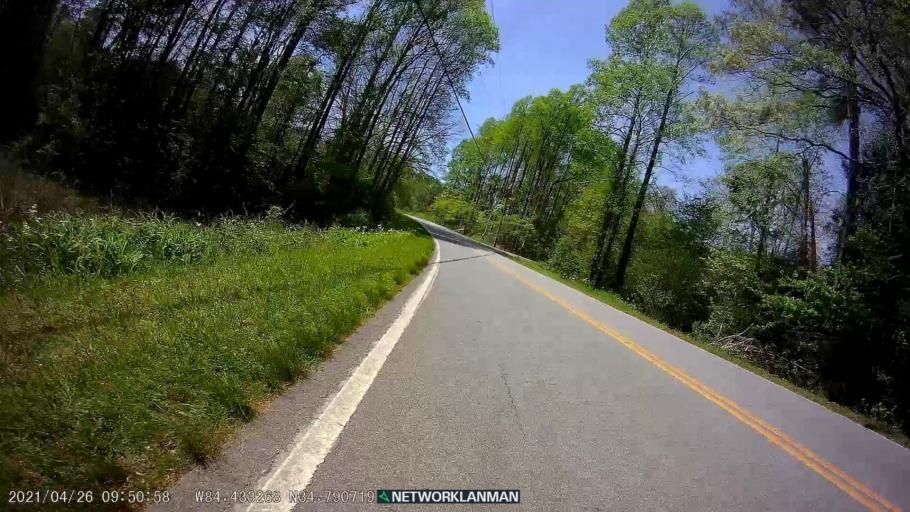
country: US
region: Georgia
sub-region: Gilmer County
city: Ellijay
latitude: 34.7914
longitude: -84.4331
